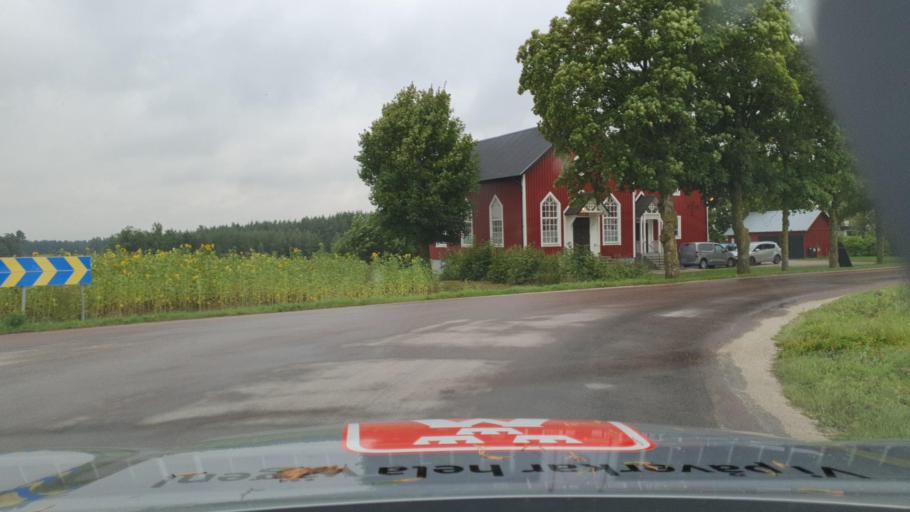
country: SE
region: Gotland
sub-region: Gotland
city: Slite
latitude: 57.6421
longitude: 18.5546
